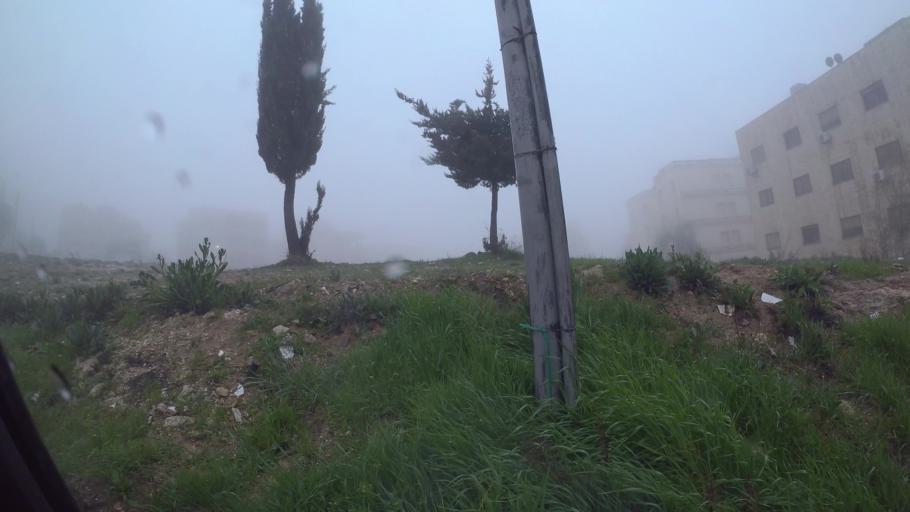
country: JO
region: Amman
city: Al Jubayhah
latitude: 32.0058
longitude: 35.8825
